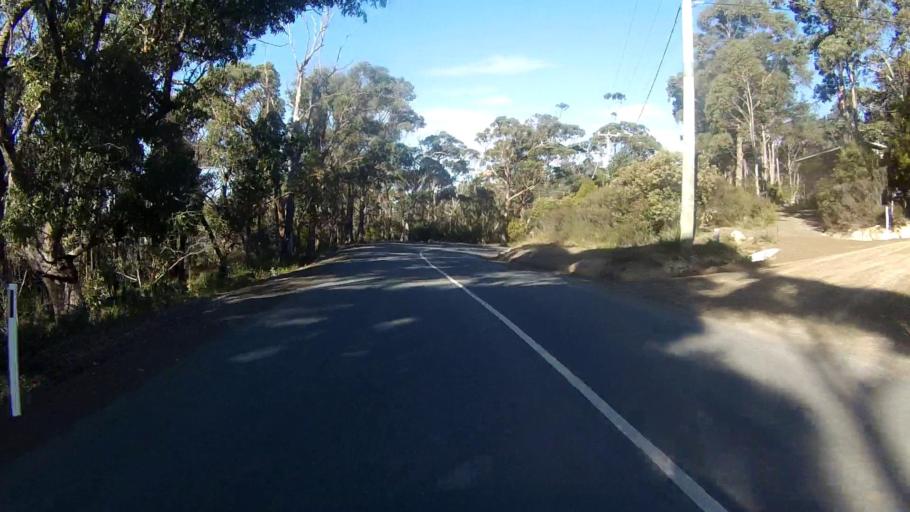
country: AU
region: Tasmania
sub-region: Clarence
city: Sandford
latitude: -43.0282
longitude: 147.9270
